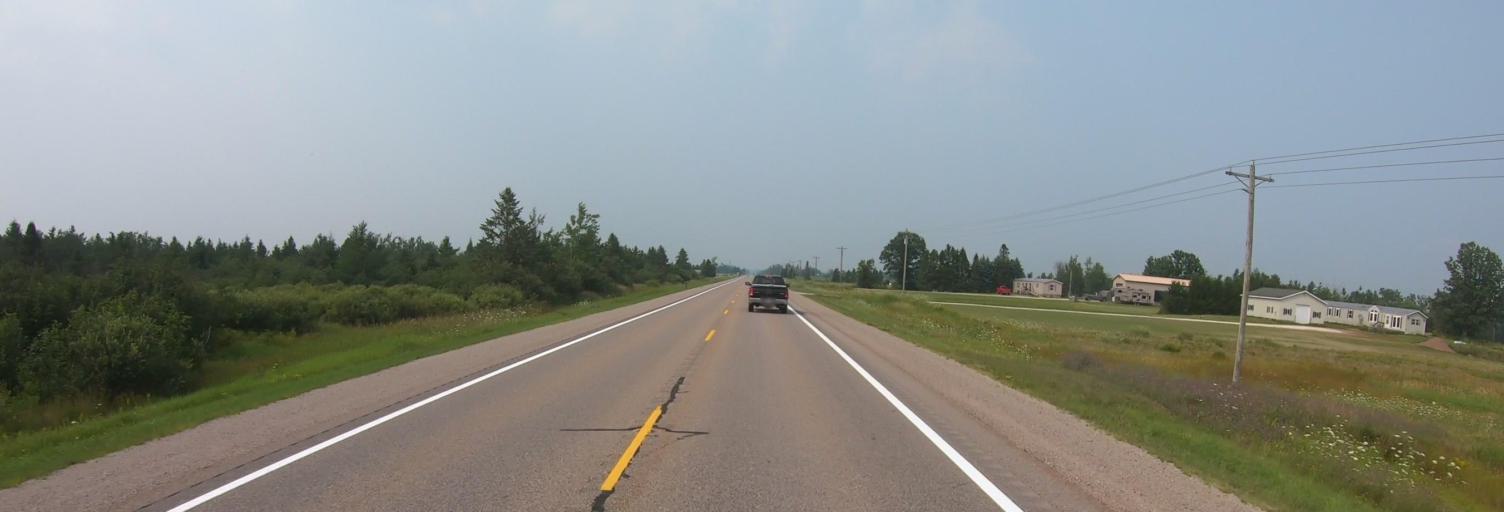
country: US
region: Michigan
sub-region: Chippewa County
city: Sault Ste. Marie
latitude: 46.3209
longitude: -84.3638
